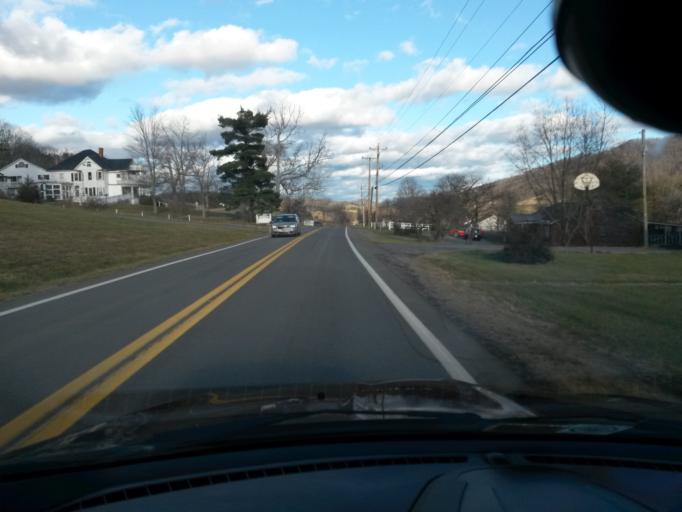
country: US
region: Virginia
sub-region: Giles County
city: Pearisburg
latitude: 37.4130
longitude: -80.7507
